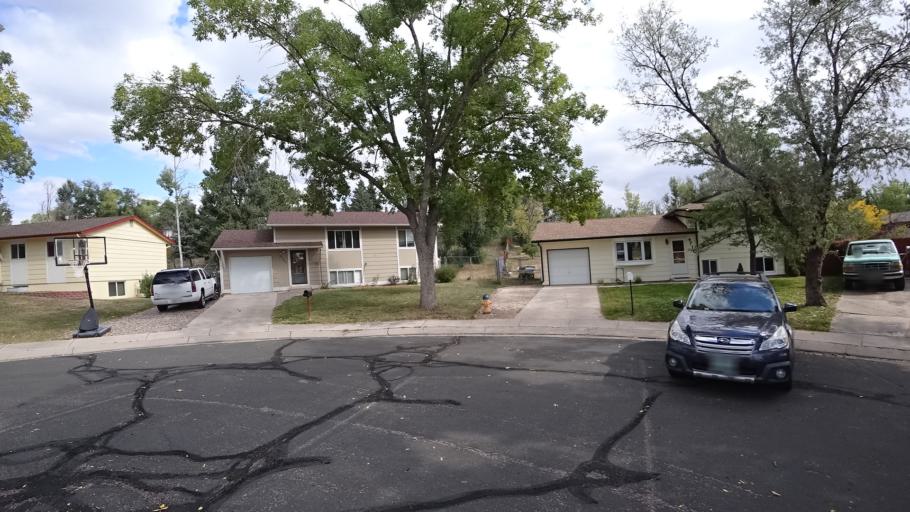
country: US
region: Colorado
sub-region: El Paso County
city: Cimarron Hills
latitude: 38.8814
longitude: -104.7401
